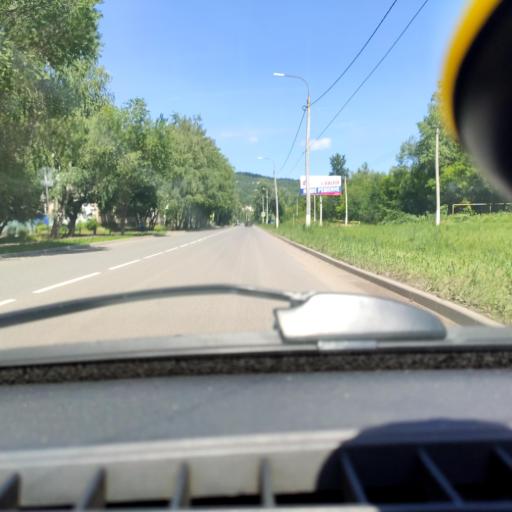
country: RU
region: Samara
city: Zhigulevsk
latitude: 53.4004
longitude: 49.5107
